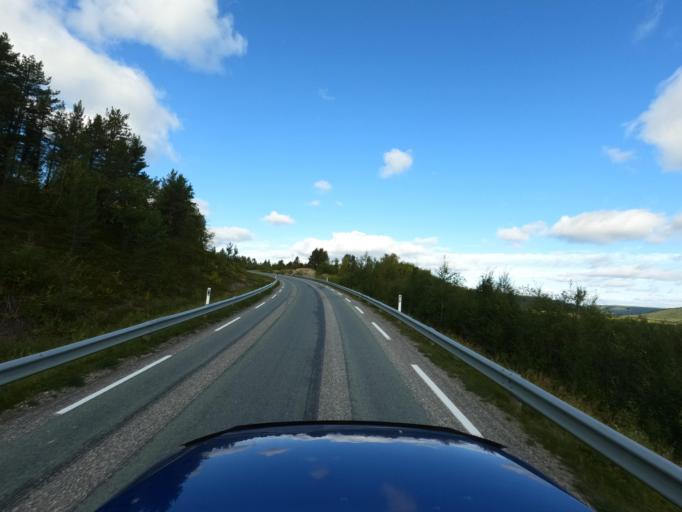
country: NO
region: Finnmark Fylke
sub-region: Karasjok
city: Karasjohka
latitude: 69.4289
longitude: 25.7939
